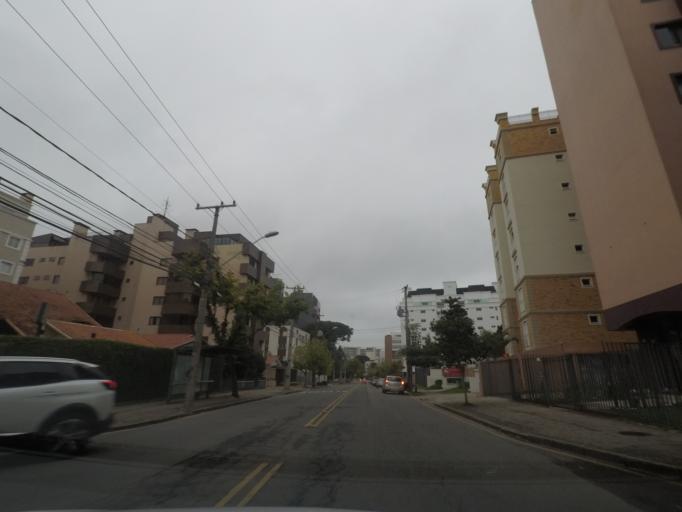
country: BR
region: Parana
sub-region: Curitiba
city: Curitiba
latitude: -25.4077
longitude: -49.2643
